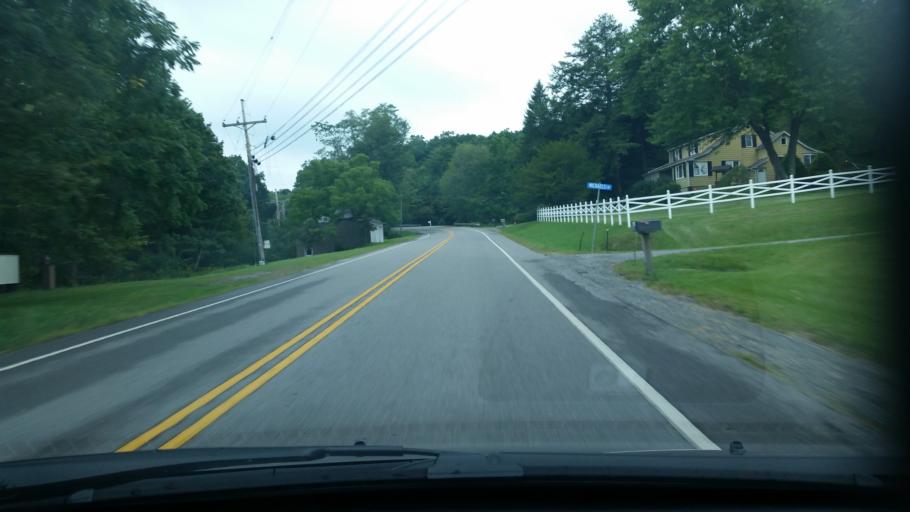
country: US
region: Pennsylvania
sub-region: Clearfield County
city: Shiloh
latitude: 41.0778
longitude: -78.3434
